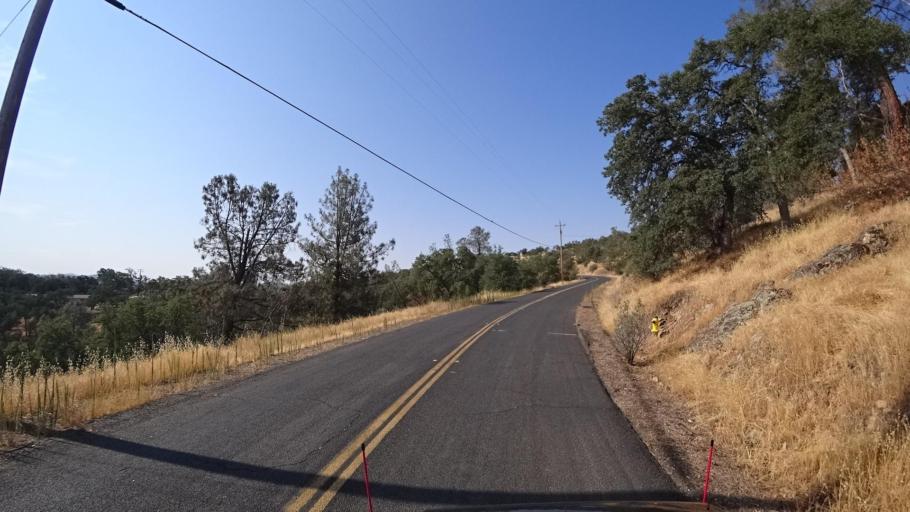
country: US
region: California
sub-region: Tuolumne County
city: Jamestown
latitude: 37.7153
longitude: -120.3361
